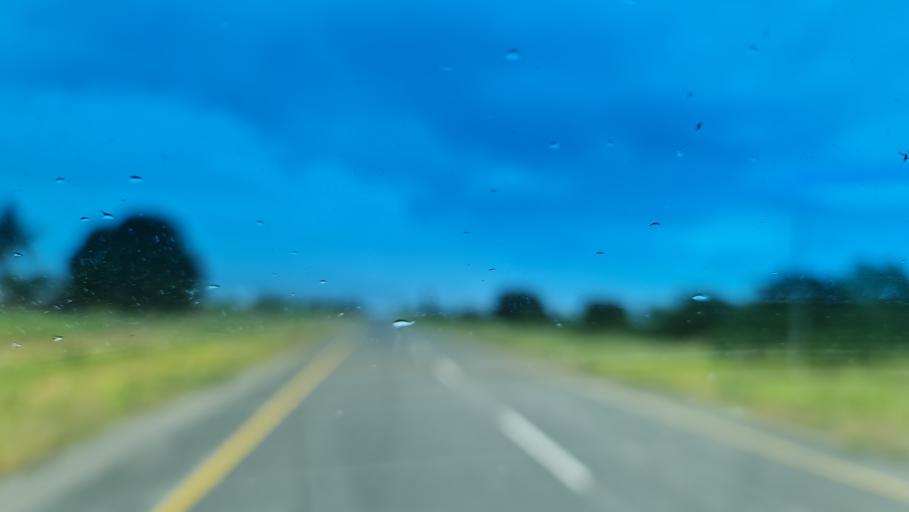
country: MZ
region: Nampula
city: Nampula
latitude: -15.5632
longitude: 39.3226
